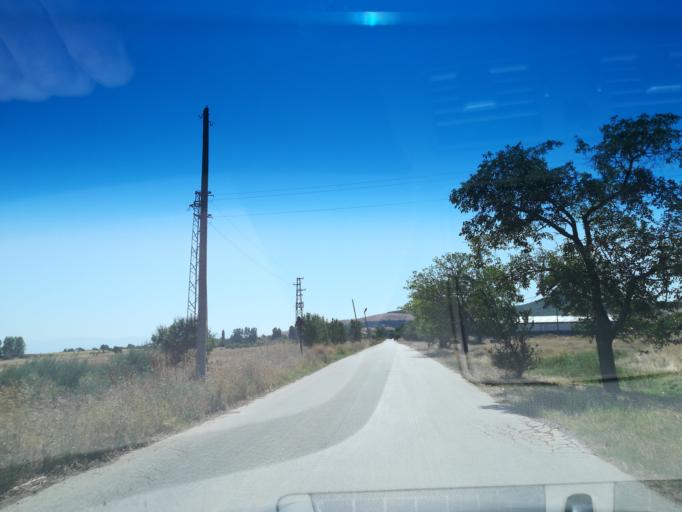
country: BG
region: Pazardzhik
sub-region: Obshtina Pazardzhik
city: Pazardzhik
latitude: 42.3457
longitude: 24.4009
